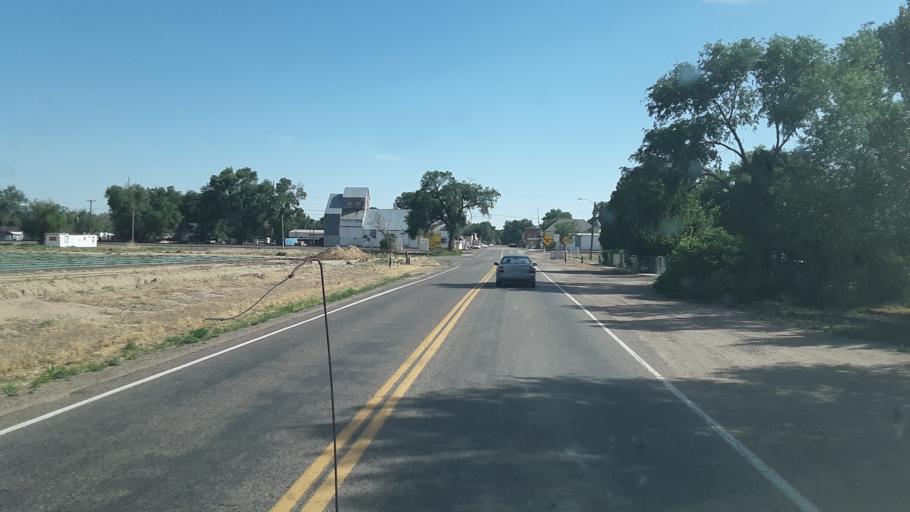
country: US
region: Colorado
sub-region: Crowley County
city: Ordway
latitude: 38.1111
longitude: -103.8652
